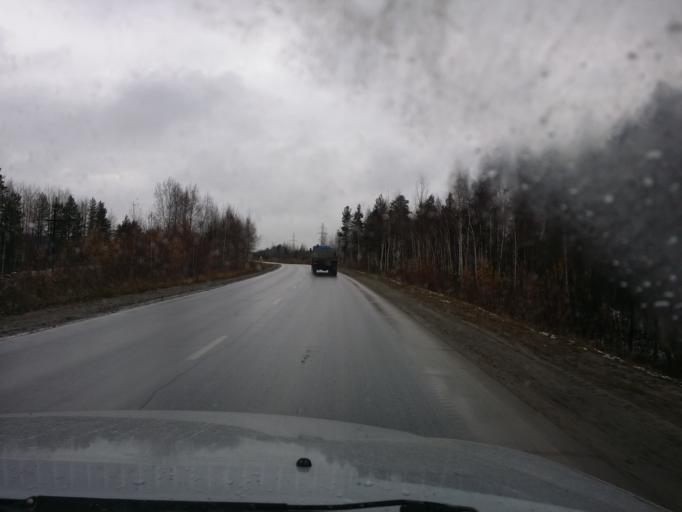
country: RU
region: Khanty-Mansiyskiy Avtonomnyy Okrug
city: Megion
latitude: 61.1430
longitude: 75.7586
